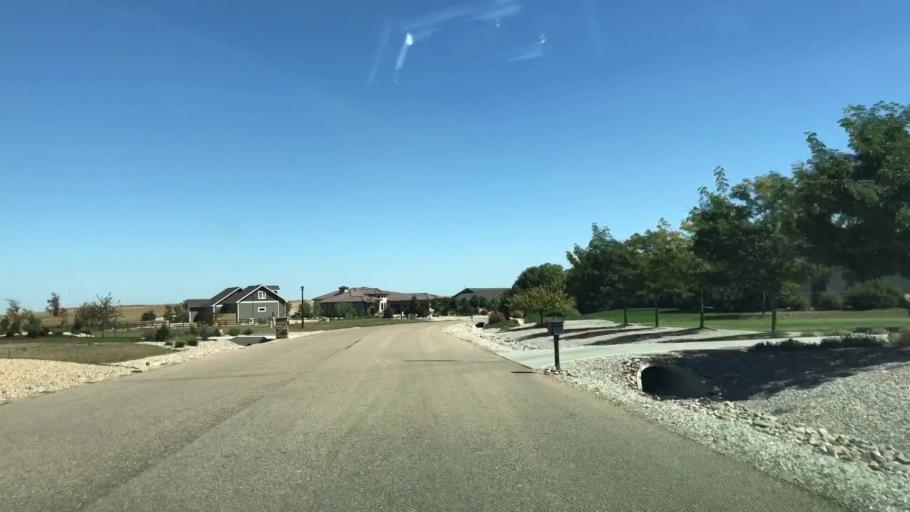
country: US
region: Colorado
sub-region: Weld County
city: Windsor
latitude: 40.4489
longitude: -104.9492
